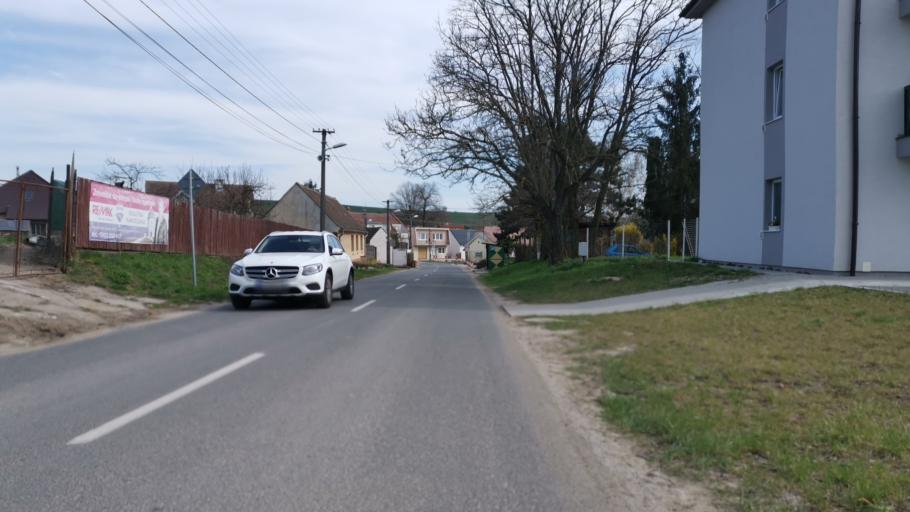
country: SK
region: Trnavsky
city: Gbely
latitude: 48.6790
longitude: 17.1305
